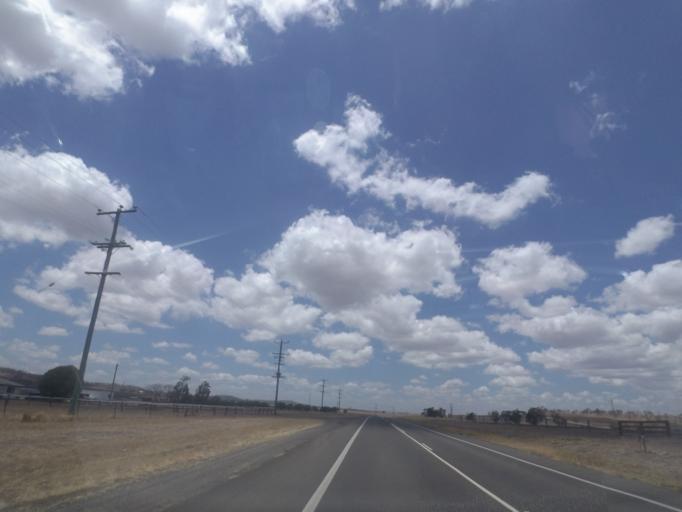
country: AU
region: Queensland
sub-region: Toowoomba
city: Top Camp
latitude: -27.7379
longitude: 151.9193
